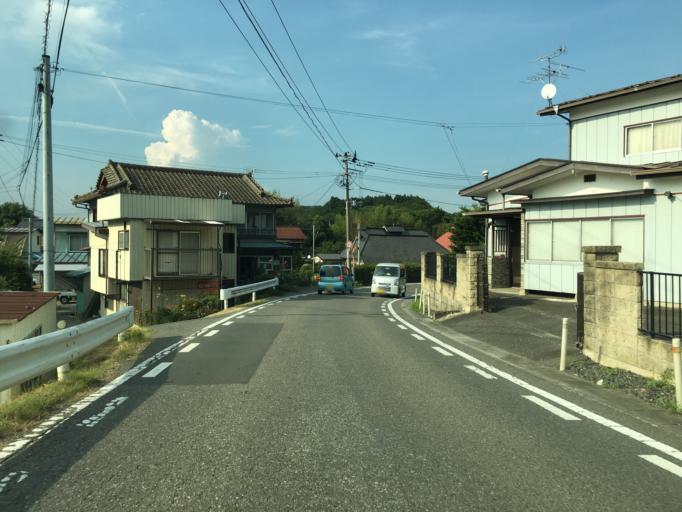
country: JP
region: Fukushima
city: Motomiya
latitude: 37.4608
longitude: 140.4240
